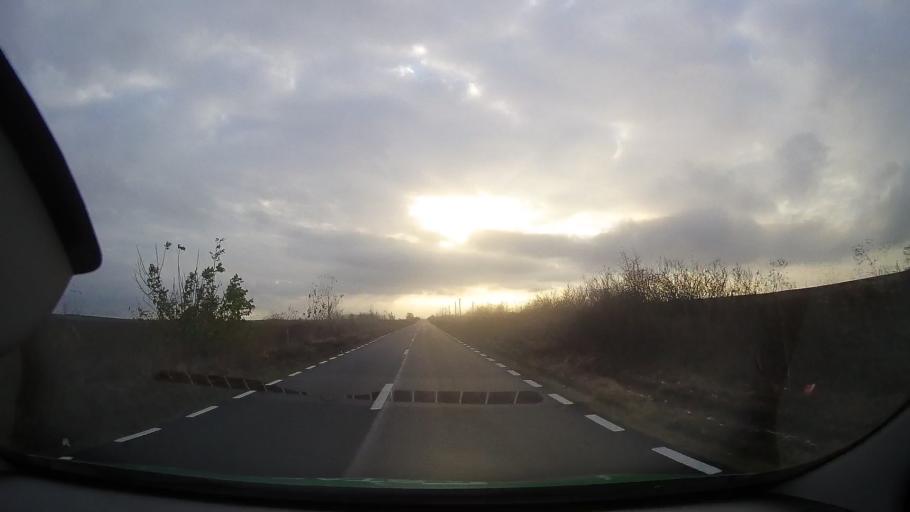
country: RO
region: Constanta
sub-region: Comuna Adamclisi
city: Adamclisi
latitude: 44.0730
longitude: 27.9859
